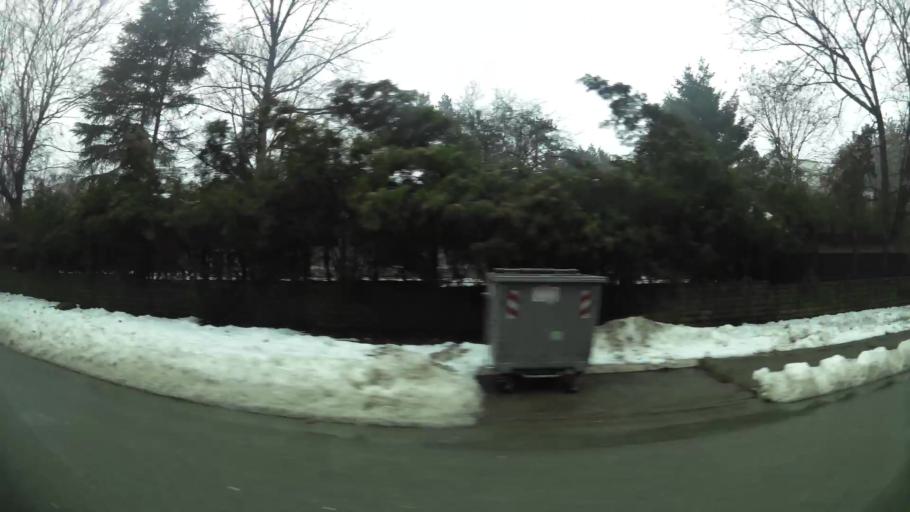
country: RS
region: Central Serbia
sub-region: Belgrade
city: Savski Venac
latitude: 44.7838
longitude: 20.4524
